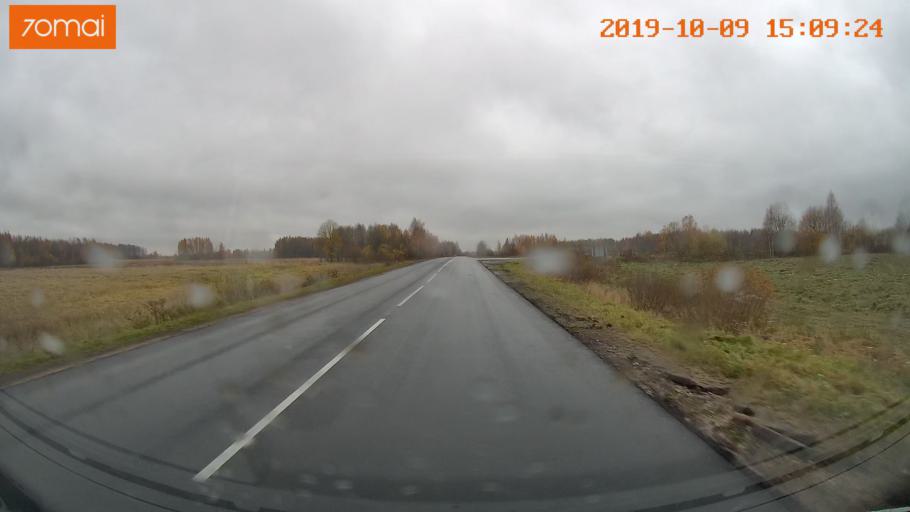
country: RU
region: Kostroma
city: Susanino
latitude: 58.1921
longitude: 41.6504
